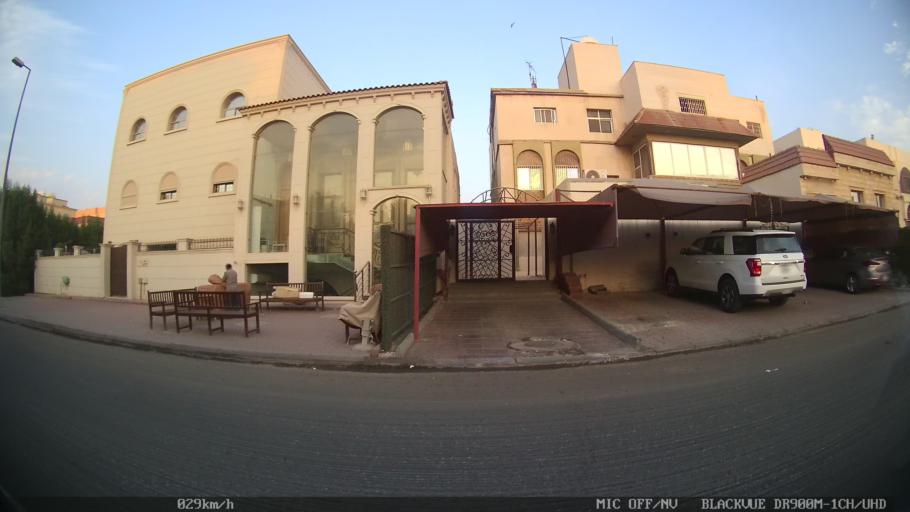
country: KW
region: Al Farwaniyah
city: Janub as Surrah
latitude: 29.2857
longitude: 47.9826
